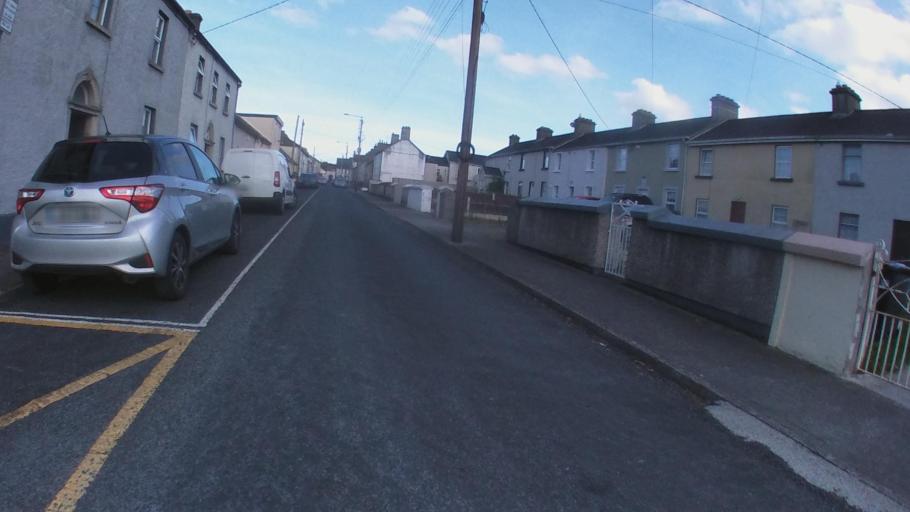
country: IE
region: Leinster
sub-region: County Carlow
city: Carlow
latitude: 52.8413
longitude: -6.9325
